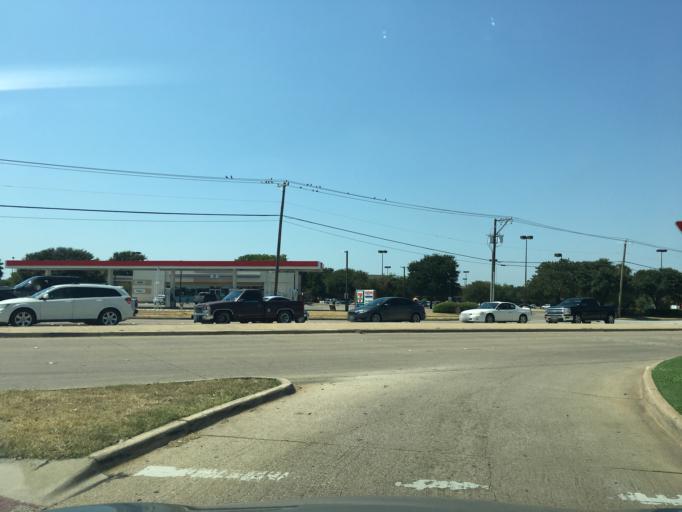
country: US
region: Texas
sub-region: Tarrant County
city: Edgecliff Village
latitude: 32.6352
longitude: -97.3694
